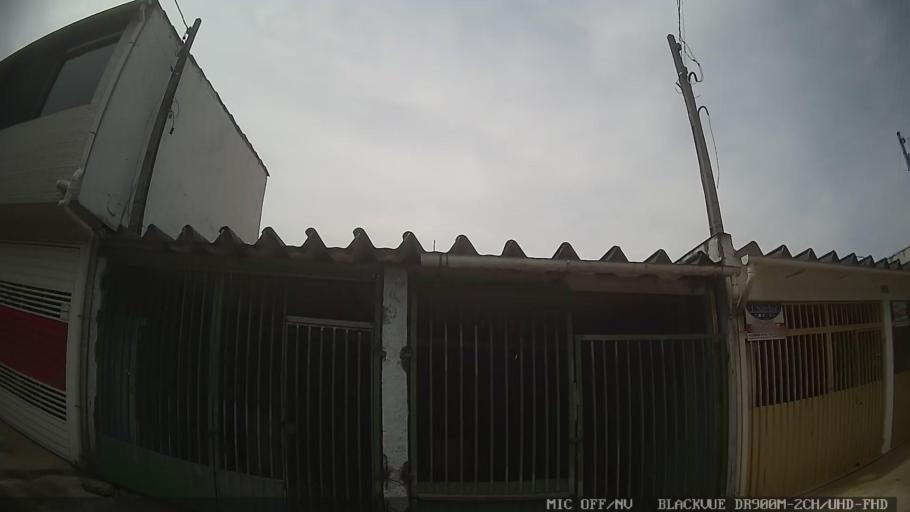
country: BR
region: Sao Paulo
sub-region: Itaquaquecetuba
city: Itaquaquecetuba
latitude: -23.4848
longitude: -46.3388
